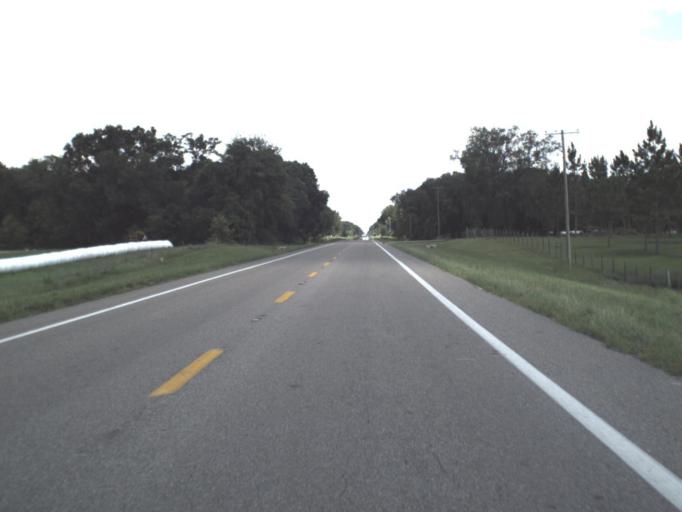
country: US
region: Florida
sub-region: Lafayette County
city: Mayo
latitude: 30.0366
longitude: -83.0677
